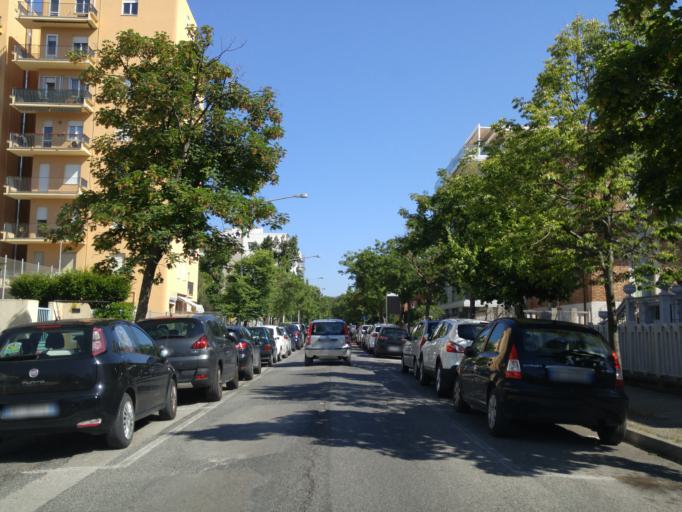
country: IT
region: The Marches
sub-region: Provincia di Pesaro e Urbino
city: Pesaro
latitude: 43.9165
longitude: 12.9126
